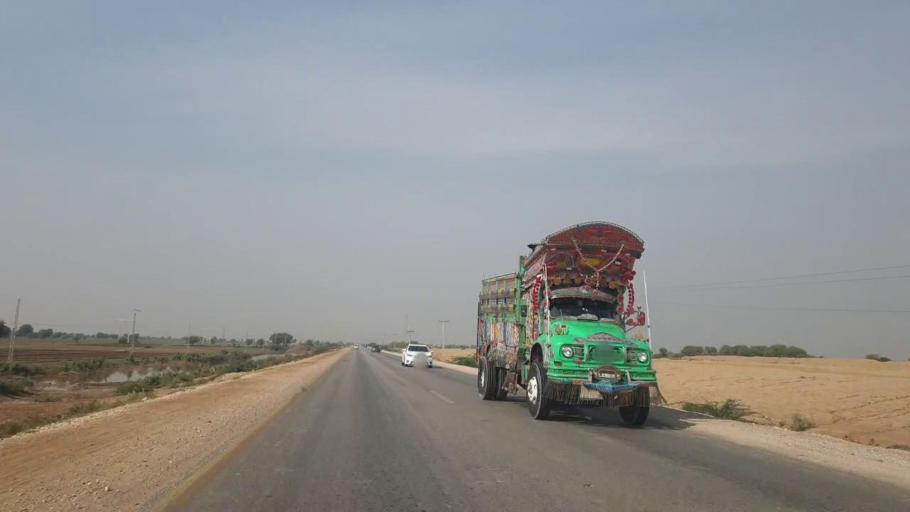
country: PK
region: Sindh
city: Sann
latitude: 26.0722
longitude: 68.0984
